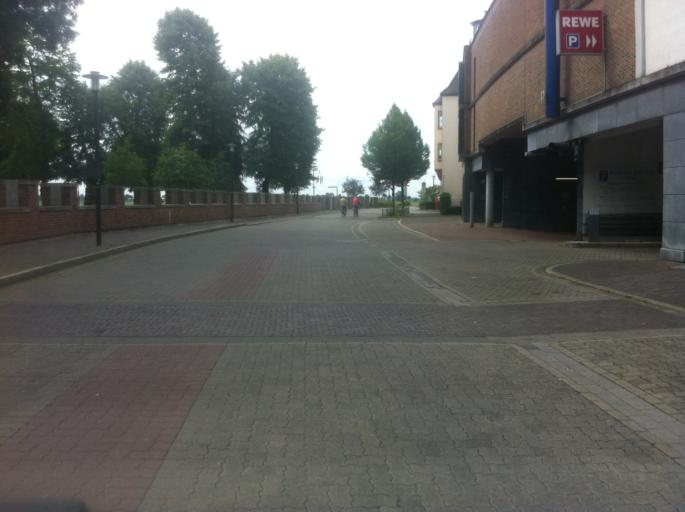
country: DE
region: North Rhine-Westphalia
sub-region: Regierungsbezirk Dusseldorf
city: Emmerich
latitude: 51.8306
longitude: 6.2471
